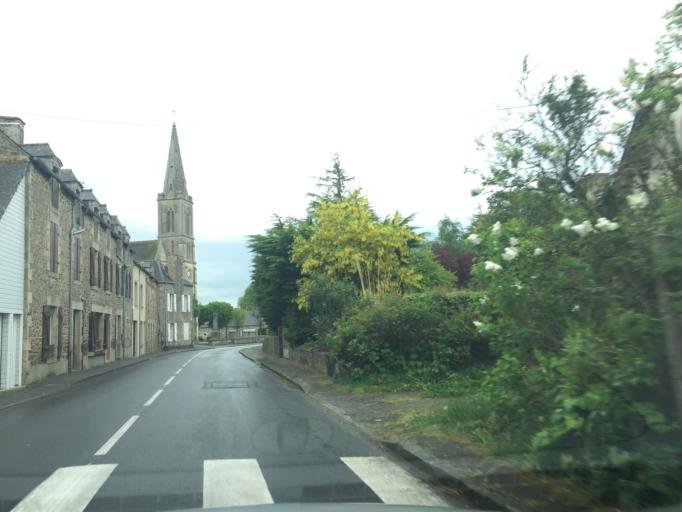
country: FR
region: Brittany
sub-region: Departement des Cotes-d'Armor
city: Crehen
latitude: 48.5465
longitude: -2.2300
